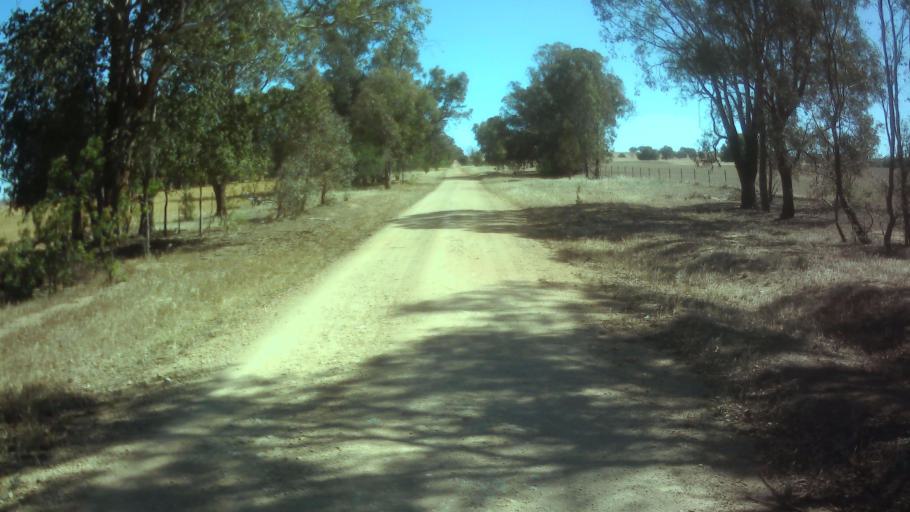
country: AU
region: New South Wales
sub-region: Weddin
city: Grenfell
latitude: -33.9908
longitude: 148.3400
